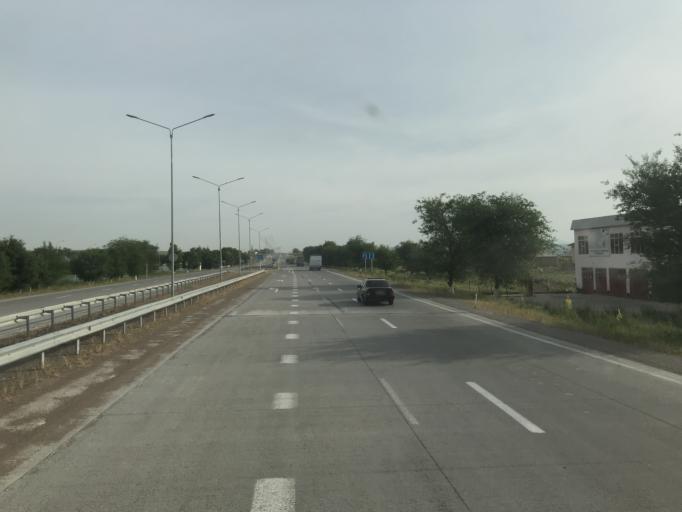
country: KZ
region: Ongtustik Qazaqstan
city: Qazyqurt
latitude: 41.7968
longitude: 69.3935
